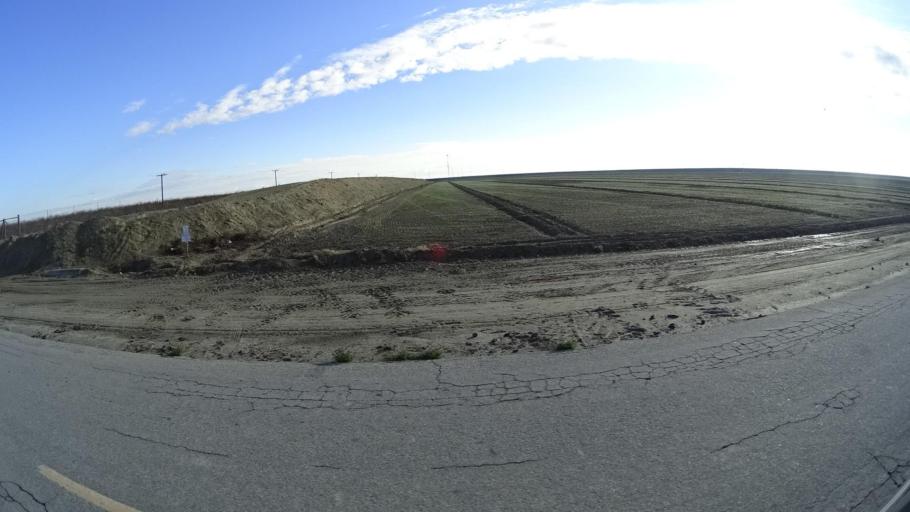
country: US
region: California
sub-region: Kern County
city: Delano
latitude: 35.7534
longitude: -119.3299
